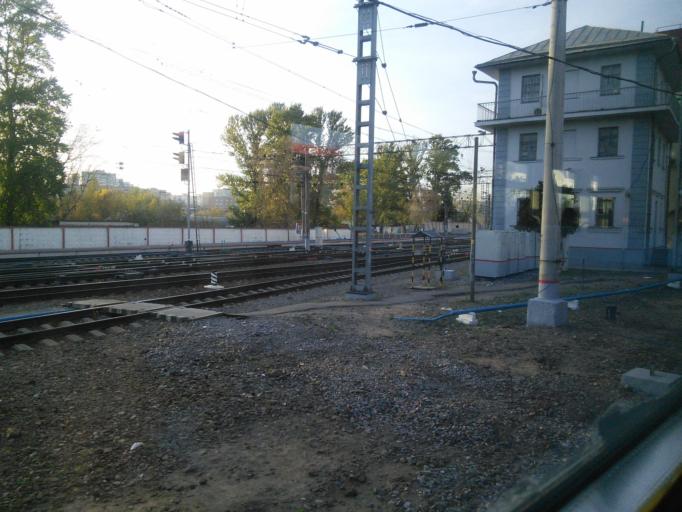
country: RU
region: Moscow
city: Sokol'niki
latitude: 55.7819
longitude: 37.6519
